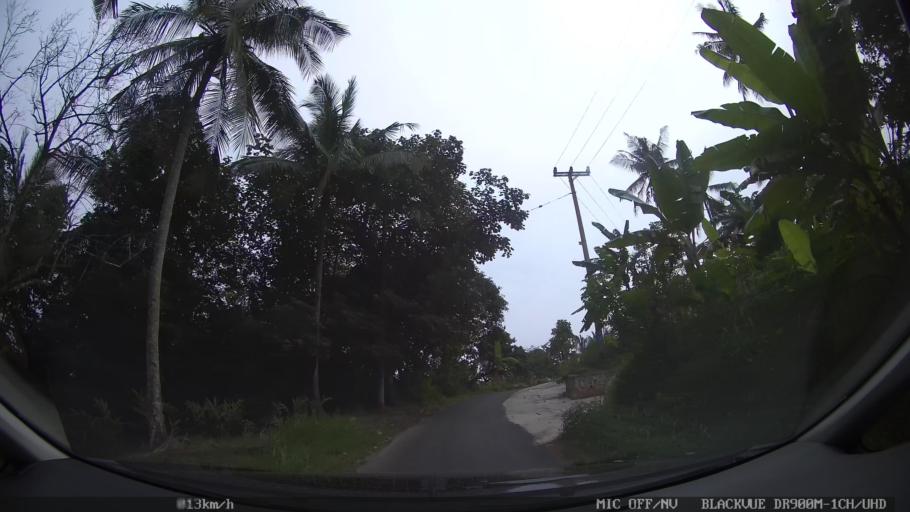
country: ID
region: Lampung
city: Bandarlampung
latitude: -5.4261
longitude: 105.3030
